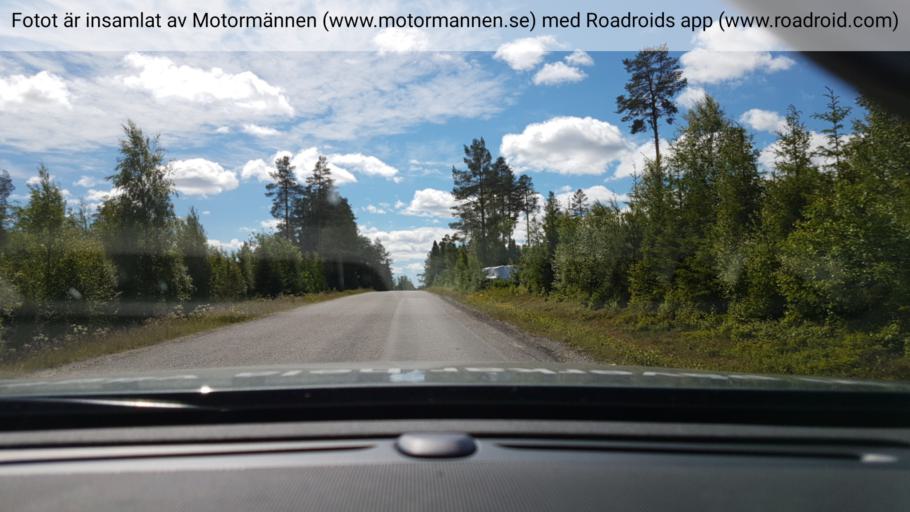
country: SE
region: Vaesterbotten
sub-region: Skelleftea Kommun
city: Burea
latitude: 64.4250
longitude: 21.3531
